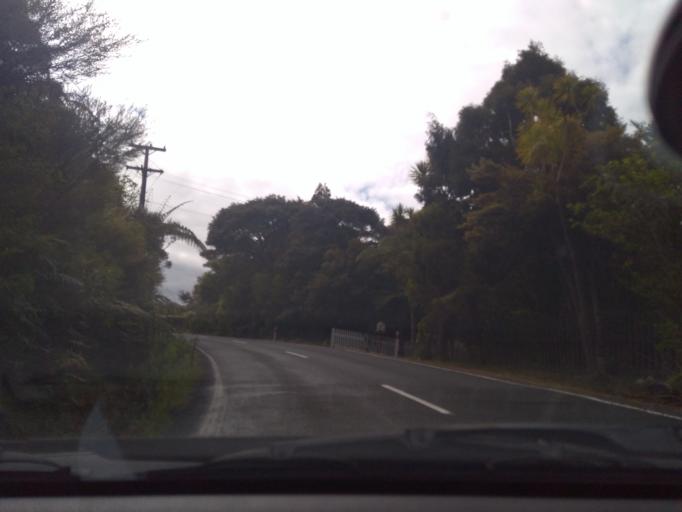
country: NZ
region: Auckland
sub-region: Auckland
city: Muriwai Beach
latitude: -36.8549
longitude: 174.4945
